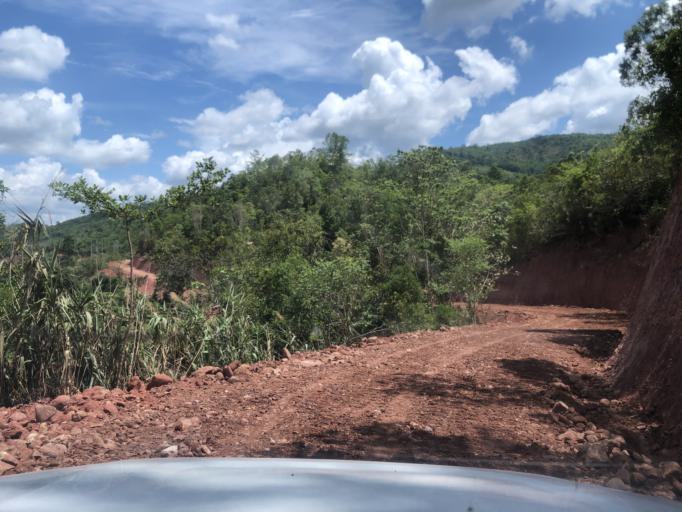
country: CN
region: Yunnan
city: Menglie
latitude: 22.2300
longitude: 101.6204
